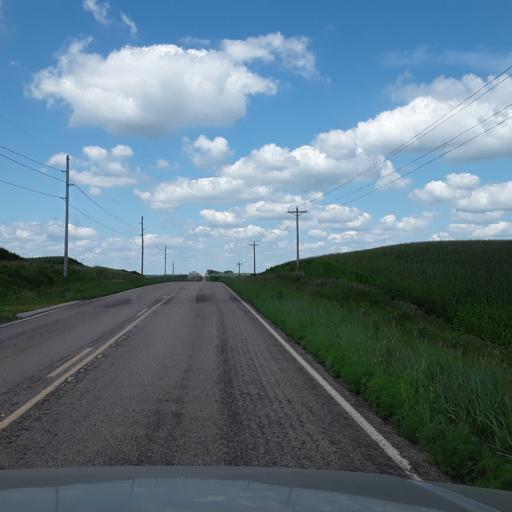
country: US
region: Nebraska
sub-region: Nance County
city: Genoa
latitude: 41.5350
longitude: -97.6960
